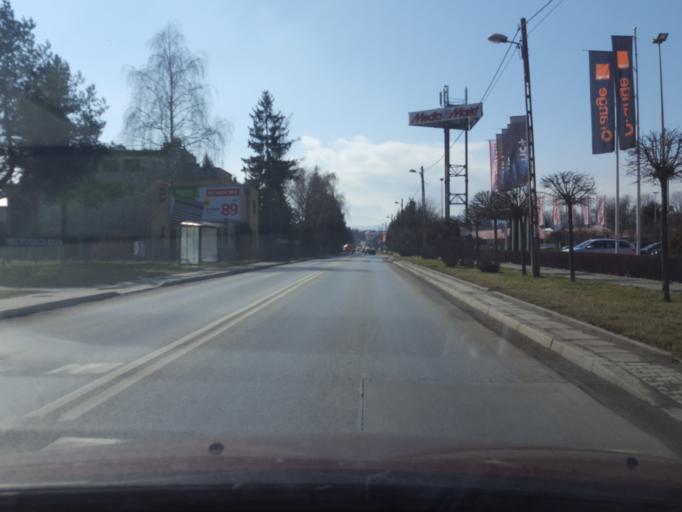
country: PL
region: Lesser Poland Voivodeship
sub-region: Powiat nowosadecki
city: Nowy Sacz
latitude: 49.6360
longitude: 20.6924
